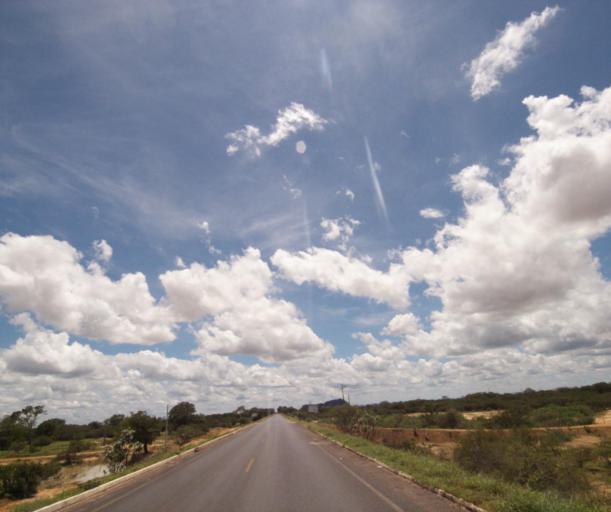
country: BR
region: Bahia
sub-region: Bom Jesus Da Lapa
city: Bom Jesus da Lapa
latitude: -13.2570
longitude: -43.4564
